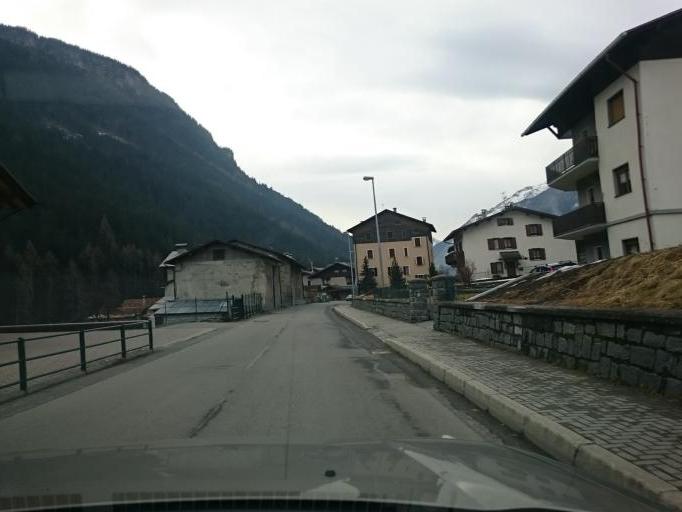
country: IT
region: Lombardy
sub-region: Provincia di Sondrio
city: Valdisotto
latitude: 46.4351
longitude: 10.3578
